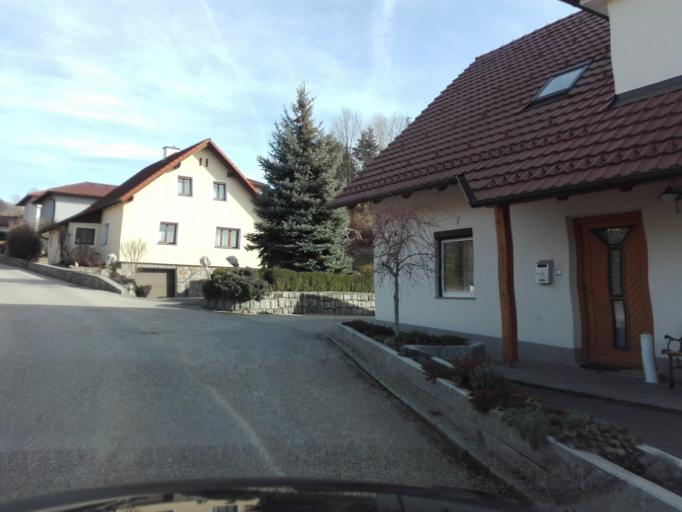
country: AT
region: Upper Austria
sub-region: Politischer Bezirk Perg
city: Perg
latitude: 48.2571
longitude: 14.5939
